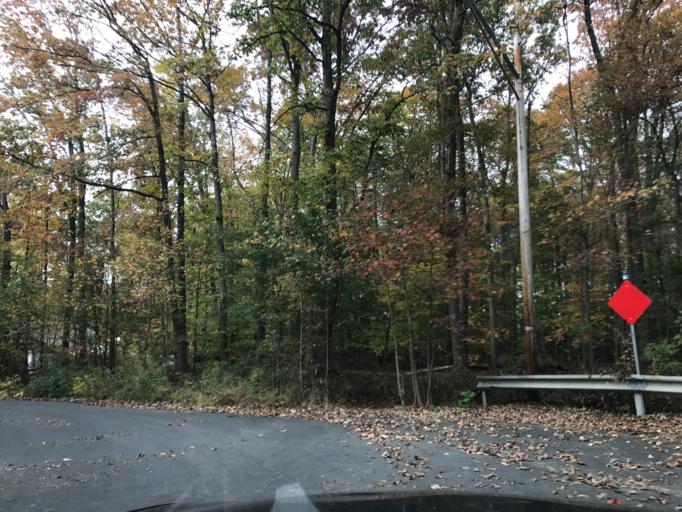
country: US
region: Maryland
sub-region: Harford County
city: Joppatowne
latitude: 39.4555
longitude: -76.3686
